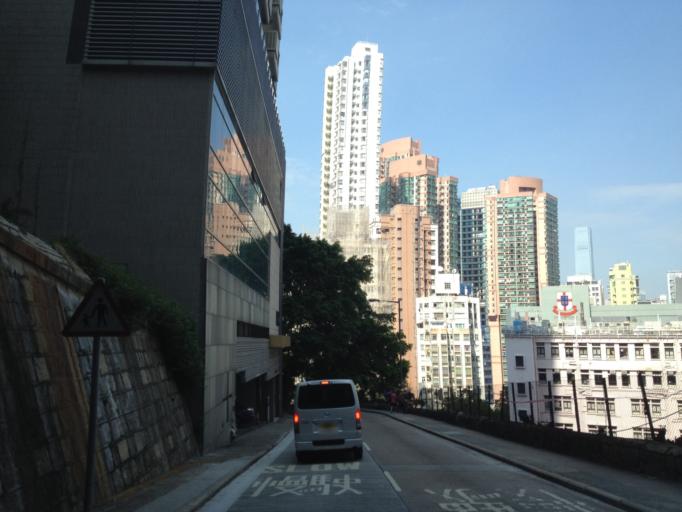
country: HK
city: Hong Kong
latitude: 22.2845
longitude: 114.1461
